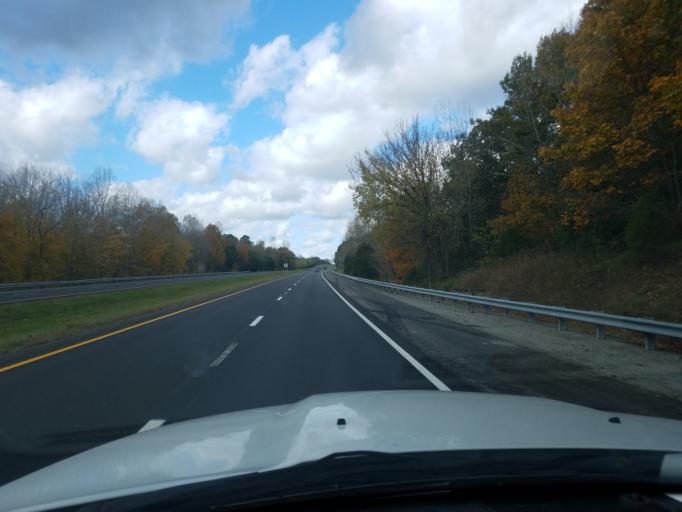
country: US
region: Kentucky
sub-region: Russell County
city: Russell Springs
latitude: 37.0649
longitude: -85.1954
